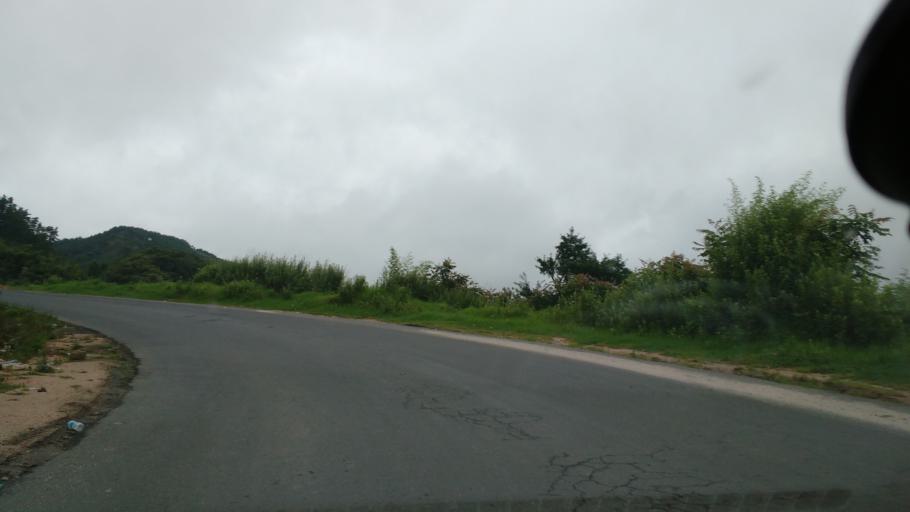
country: IN
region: Meghalaya
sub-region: East Khasi Hills
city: Shillong
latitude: 25.4916
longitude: 91.8212
